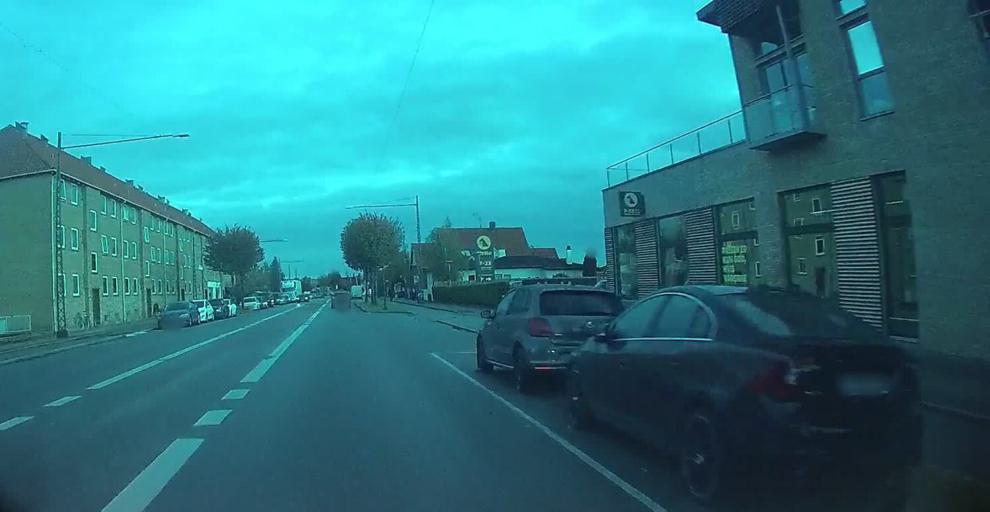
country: DK
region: Capital Region
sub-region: Tarnby Kommune
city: Tarnby
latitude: 55.6389
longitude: 12.5889
